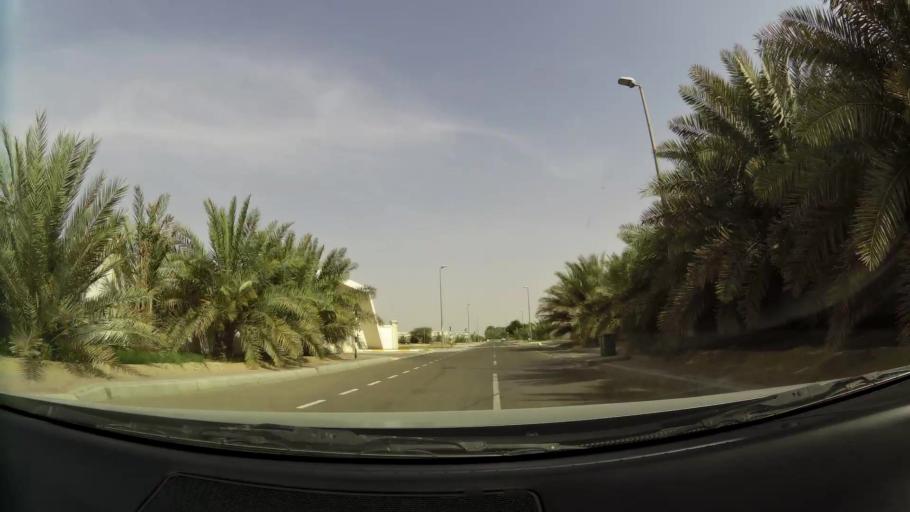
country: AE
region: Abu Dhabi
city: Al Ain
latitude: 24.1526
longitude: 55.7059
